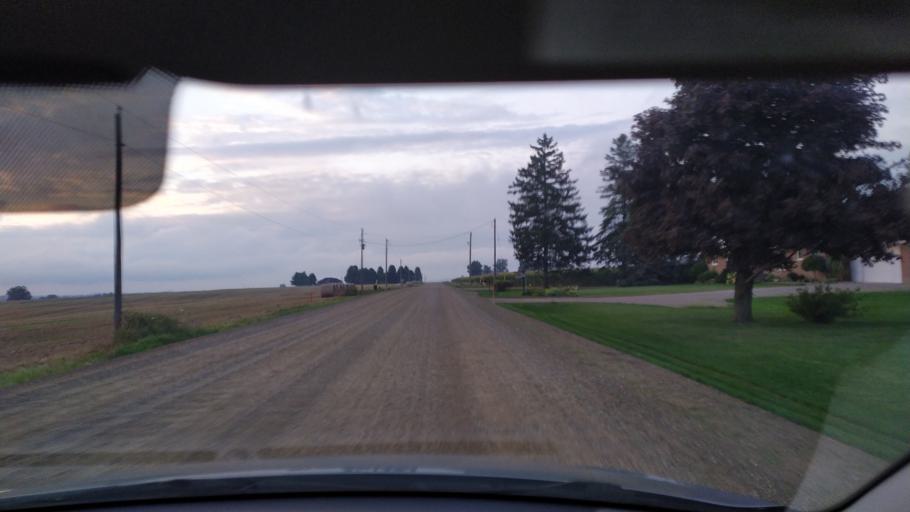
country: CA
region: Ontario
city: Kitchener
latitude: 43.3123
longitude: -80.6122
